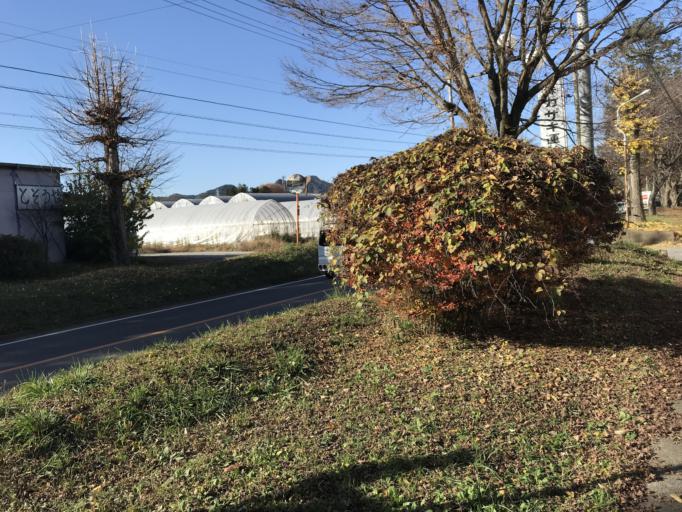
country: JP
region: Tochigi
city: Kanuma
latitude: 36.5990
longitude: 139.7440
